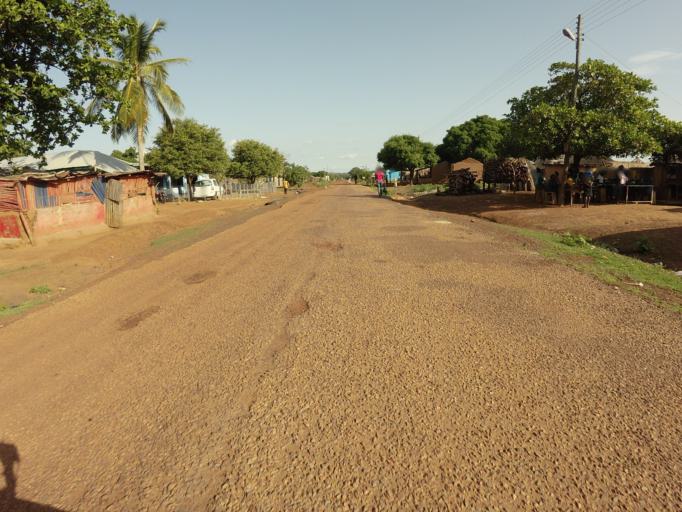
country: GH
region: Upper East
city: Bawku
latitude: 10.6289
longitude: -0.1800
